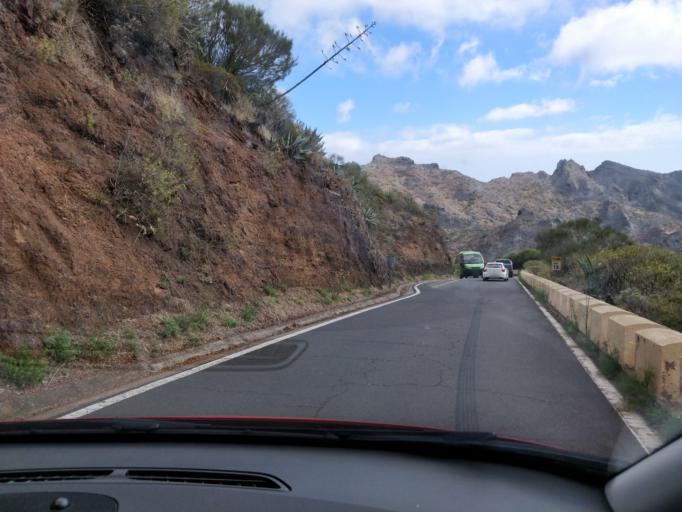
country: ES
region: Canary Islands
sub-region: Provincia de Santa Cruz de Tenerife
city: Santiago del Teide
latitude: 28.3219
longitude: -16.8560
